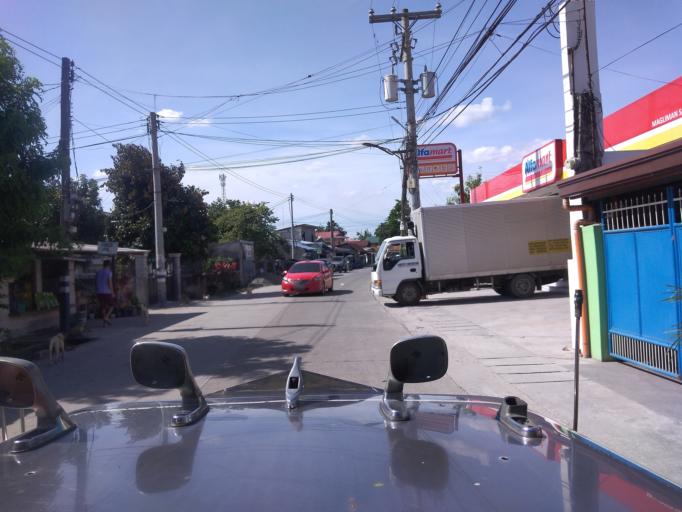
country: PH
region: Central Luzon
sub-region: Province of Pampanga
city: Magliman
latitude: 15.0362
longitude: 120.6627
